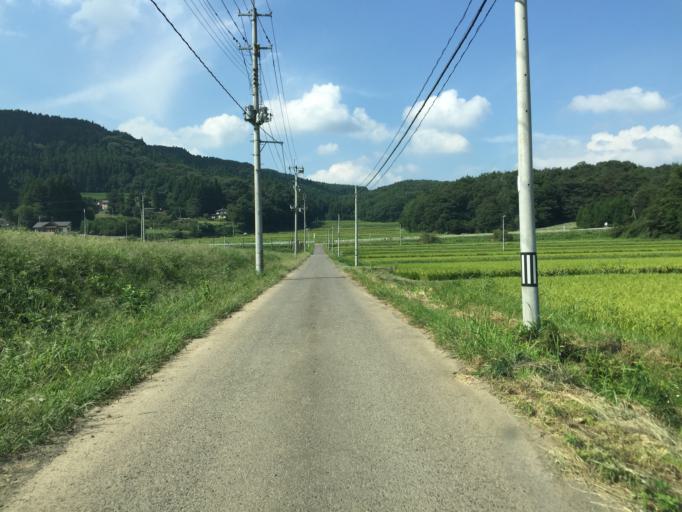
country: JP
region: Fukushima
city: Nihommatsu
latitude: 37.5978
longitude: 140.3846
